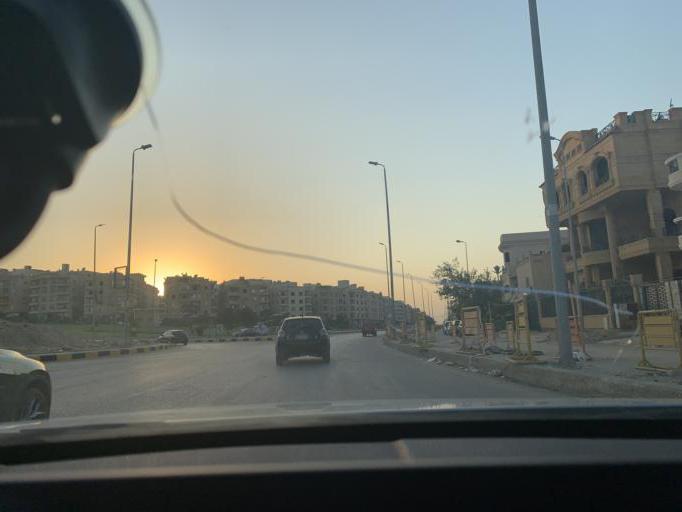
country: EG
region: Muhafazat al Qahirah
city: Cairo
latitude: 29.9997
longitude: 31.4636
